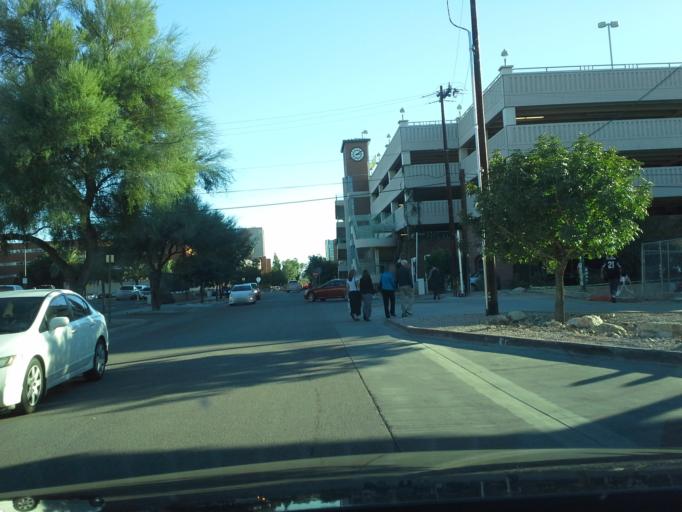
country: US
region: Arizona
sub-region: Pima County
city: Tucson
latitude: 32.2314
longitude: -110.9580
